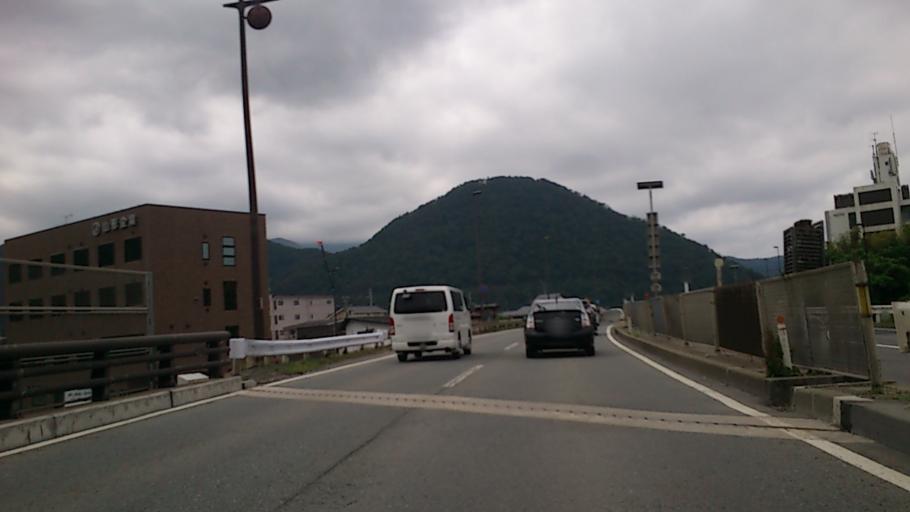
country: JP
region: Yamagata
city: Yamagata-shi
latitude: 38.2488
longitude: 140.3567
